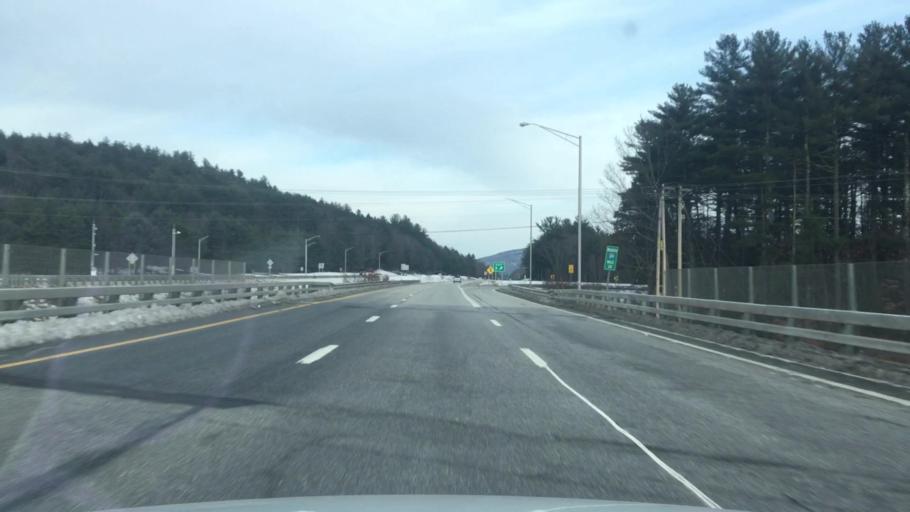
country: US
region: New Hampshire
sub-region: Merrimack County
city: Henniker
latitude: 43.2891
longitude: -71.8362
